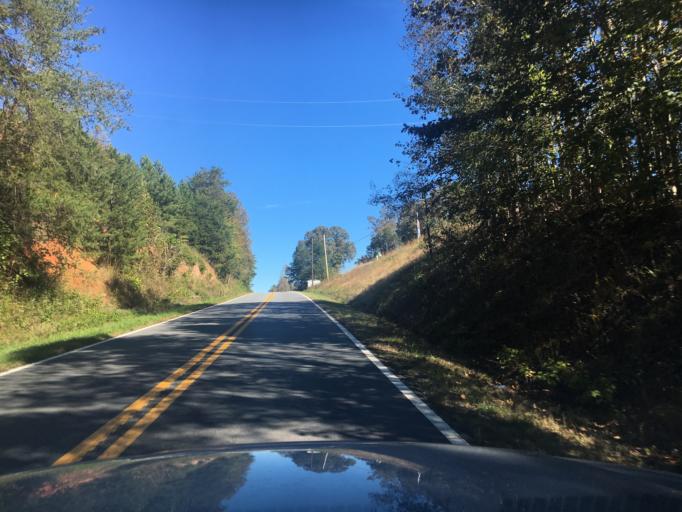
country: US
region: North Carolina
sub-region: Rutherford County
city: Spindale
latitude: 35.4766
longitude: -81.8814
